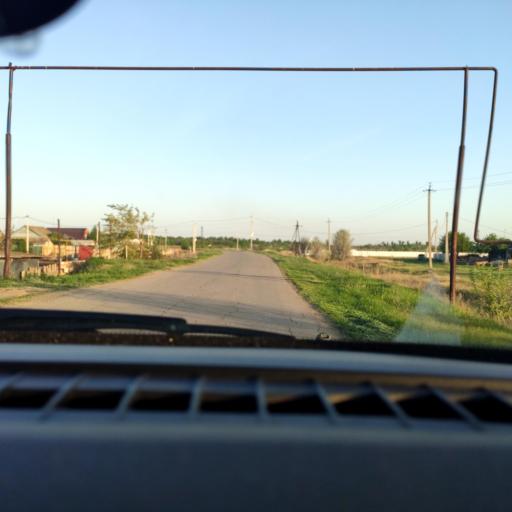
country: RU
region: Samara
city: Georgiyevka
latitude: 53.2701
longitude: 50.9587
